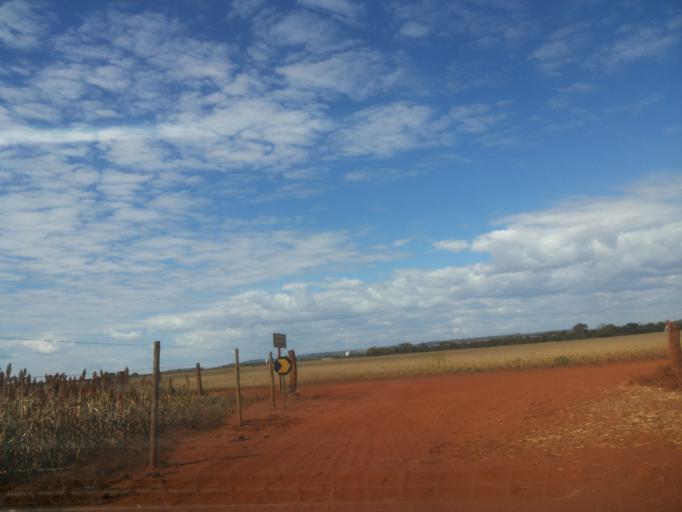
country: BR
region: Minas Gerais
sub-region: Centralina
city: Centralina
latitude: -18.5647
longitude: -49.2238
